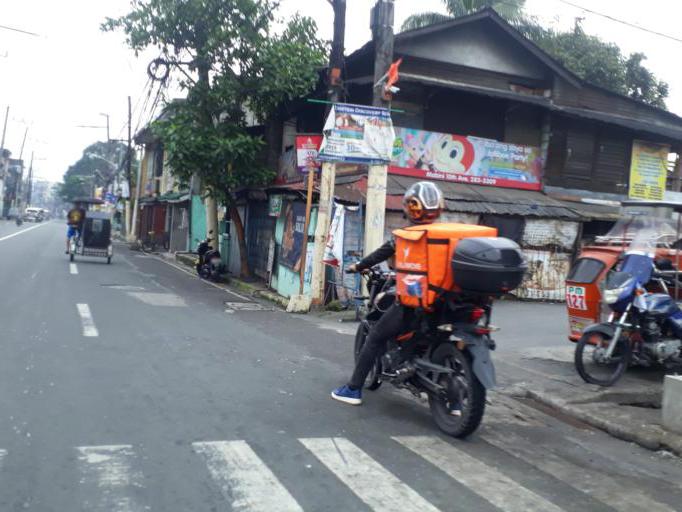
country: PH
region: Metro Manila
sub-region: Caloocan City
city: Niugan
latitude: 14.6536
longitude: 120.9721
